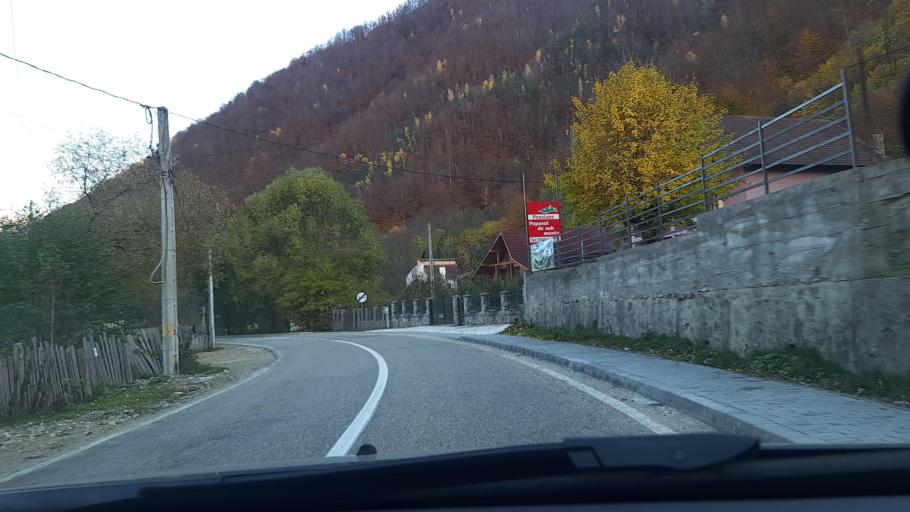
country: RO
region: Valcea
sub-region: Comuna Malaia
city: Malaia
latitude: 45.3494
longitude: 24.1409
